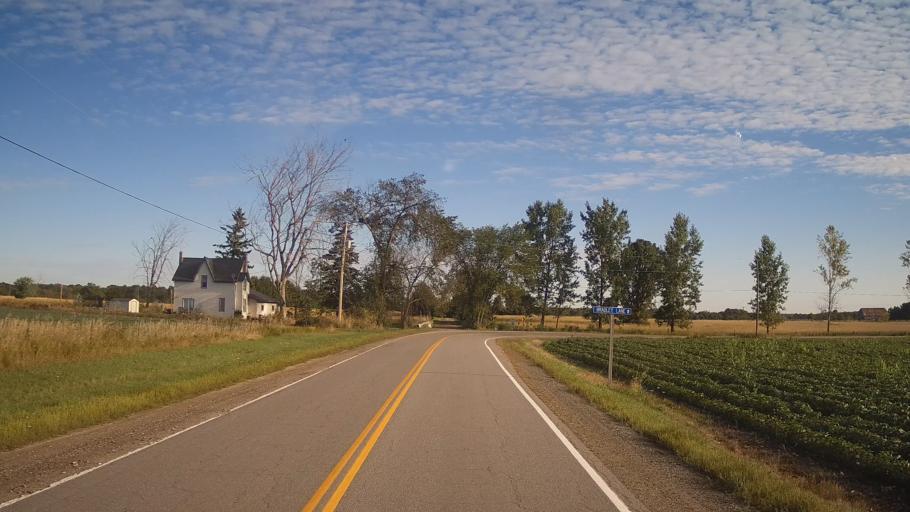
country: CA
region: Ontario
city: Gananoque
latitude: 44.3987
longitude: -76.1101
